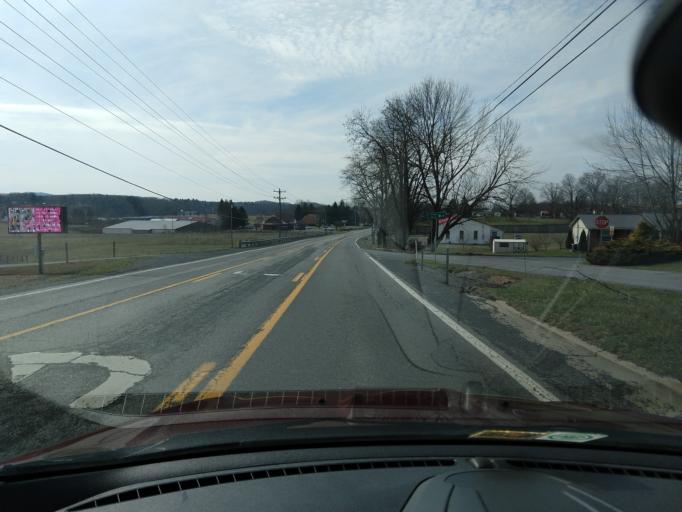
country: US
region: West Virginia
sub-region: Greenbrier County
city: Lewisburg
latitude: 37.8397
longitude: -80.4155
